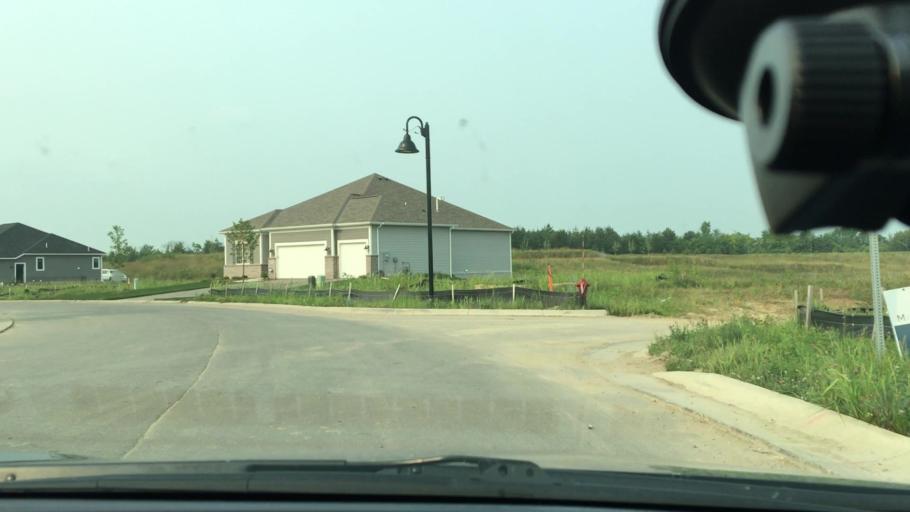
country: US
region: Minnesota
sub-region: Anoka County
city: Ramsey
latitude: 45.2188
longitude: -93.4639
